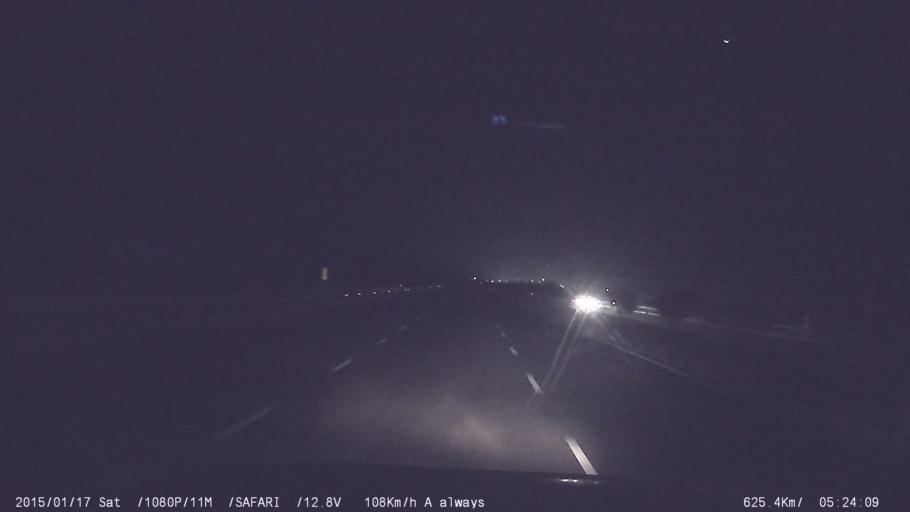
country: IN
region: Tamil Nadu
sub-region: Vellore
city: Katpadi
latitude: 12.9476
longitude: 79.2156
